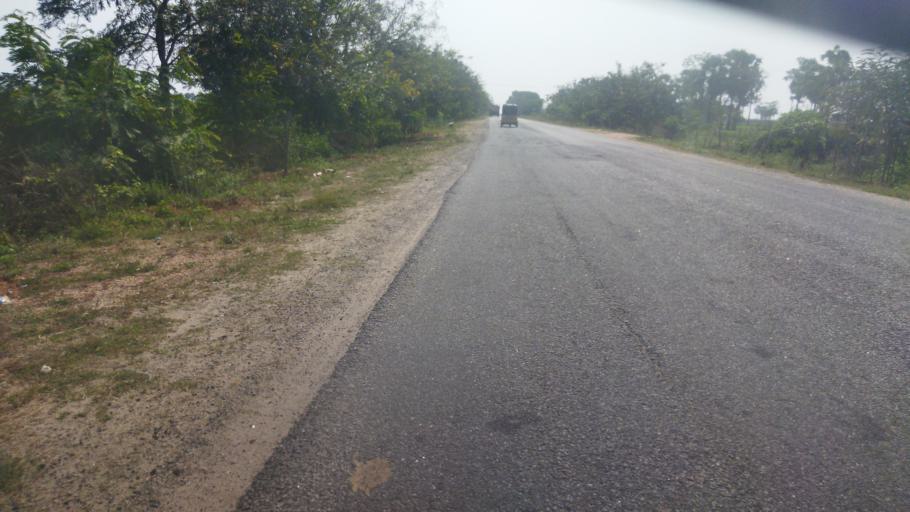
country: IN
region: Telangana
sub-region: Nalgonda
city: Nalgonda
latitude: 17.1052
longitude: 79.2812
